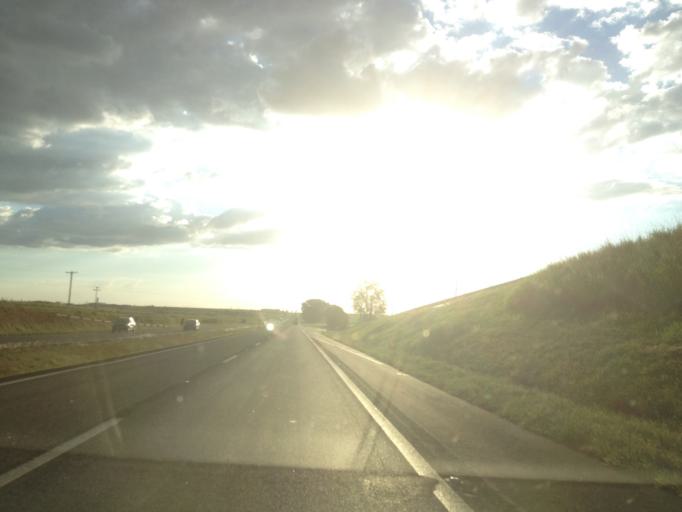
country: BR
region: Sao Paulo
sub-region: Jau
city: Jau
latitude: -22.2688
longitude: -48.4903
